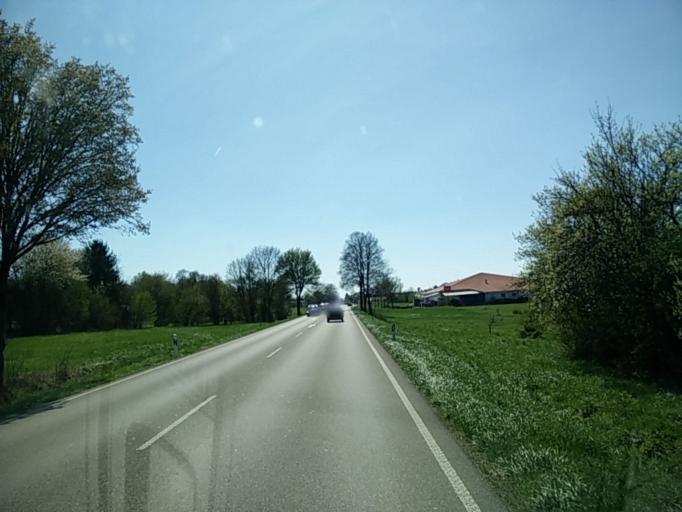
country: DE
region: Baden-Wuerttemberg
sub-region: Tuebingen Region
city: Ofterdingen
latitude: 48.4247
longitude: 9.0443
